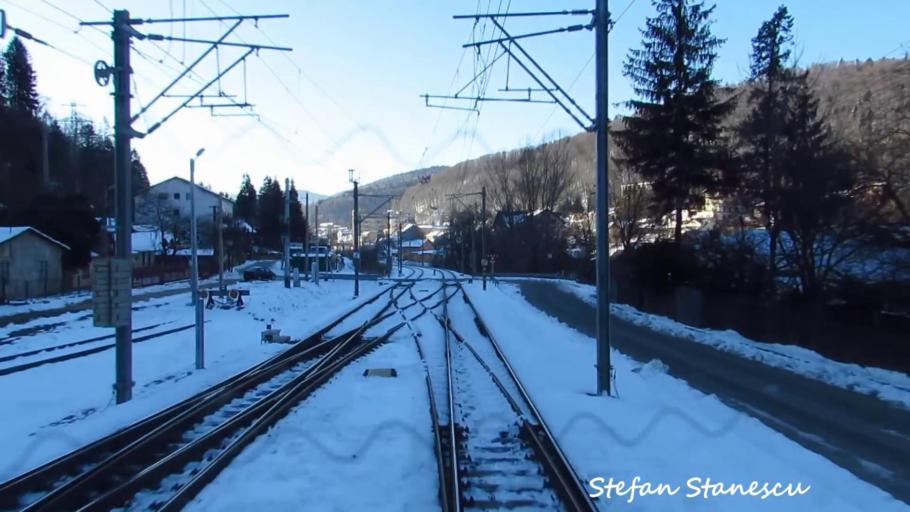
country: RO
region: Prahova
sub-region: Oras Sinaia
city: Sinaia
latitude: 45.3464
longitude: 25.5508
